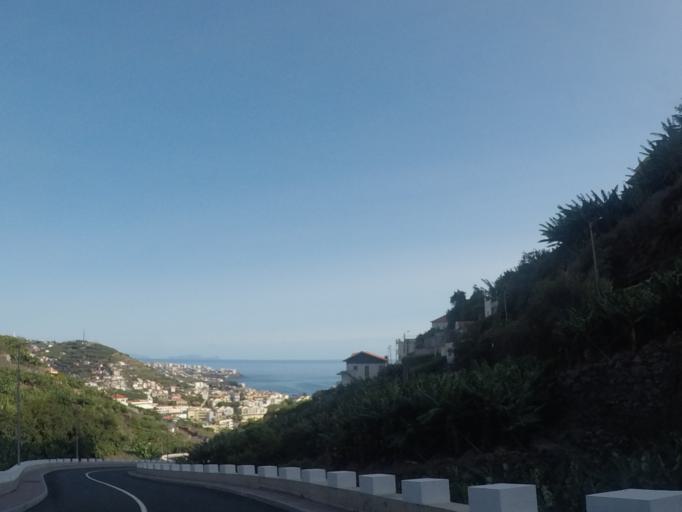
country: PT
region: Madeira
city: Camara de Lobos
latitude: 32.6563
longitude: -16.9902
